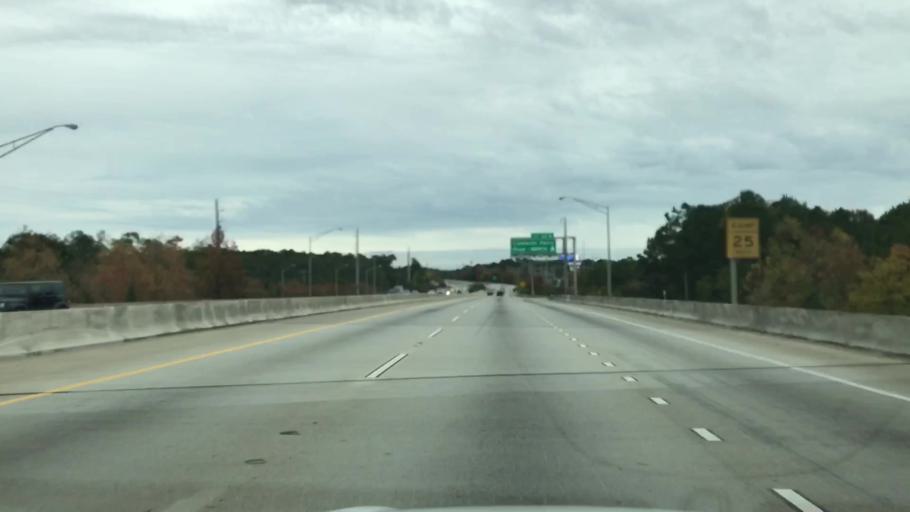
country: US
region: South Carolina
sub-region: Charleston County
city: North Charleston
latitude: 32.8788
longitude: -79.9313
